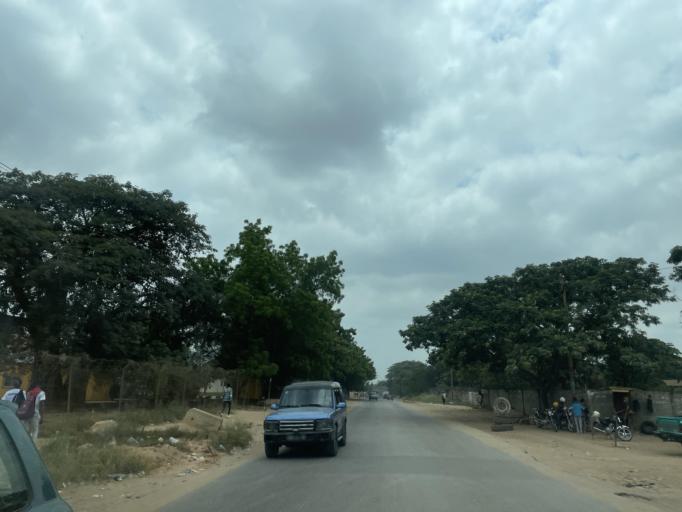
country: AO
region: Luanda
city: Luanda
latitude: -8.9144
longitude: 13.3766
